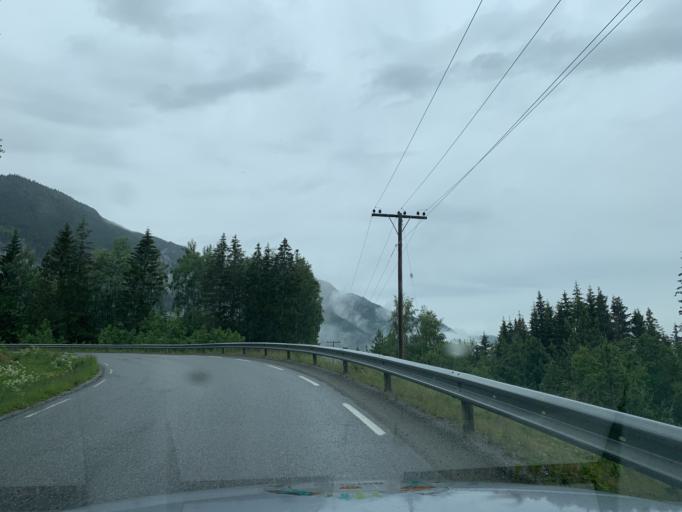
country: NO
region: Oppland
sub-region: Ringebu
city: Ringebu
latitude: 61.4488
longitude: 10.1777
